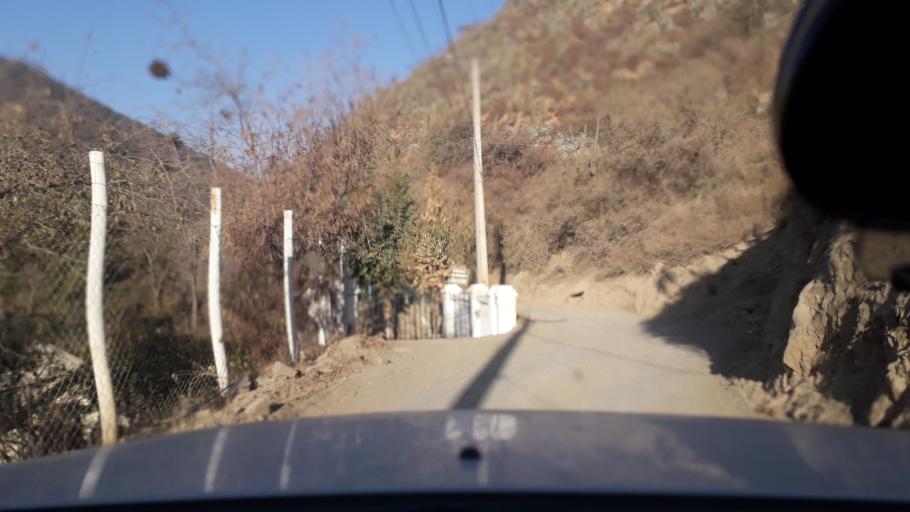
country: CL
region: Valparaiso
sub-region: Provincia de Marga Marga
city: Limache
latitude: -33.0516
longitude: -71.0862
